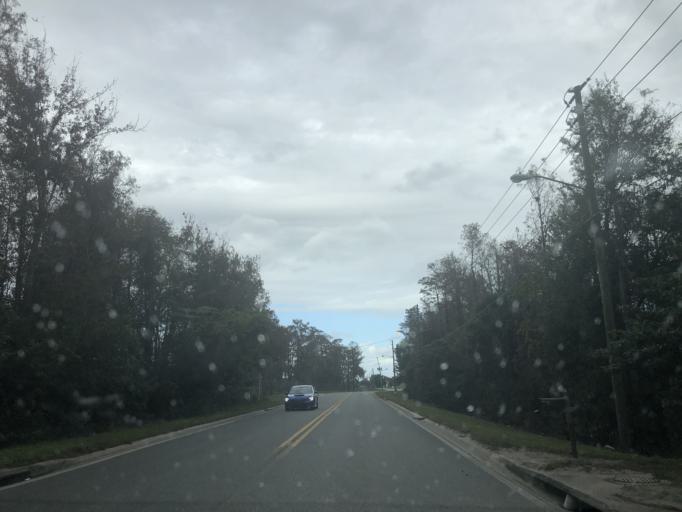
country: US
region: Florida
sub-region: Orange County
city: Southchase
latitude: 28.4120
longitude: -81.3882
